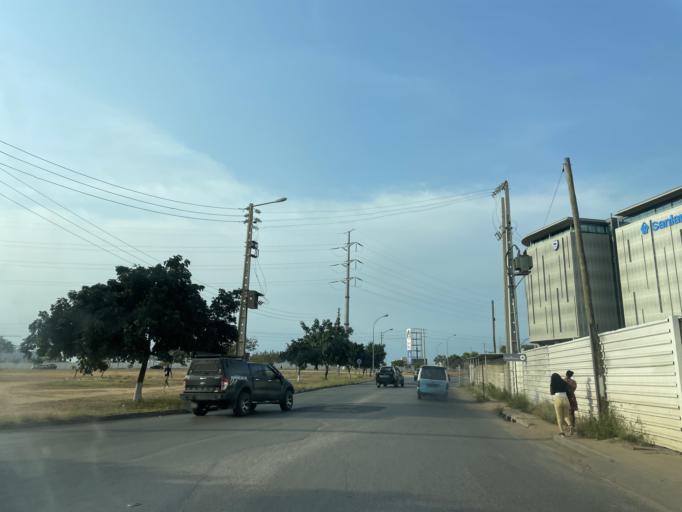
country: AO
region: Luanda
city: Luanda
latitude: -8.9210
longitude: 13.1920
